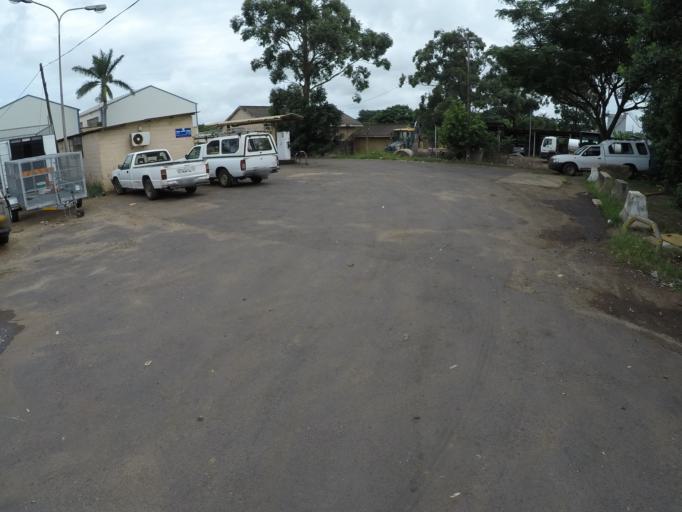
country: ZA
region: KwaZulu-Natal
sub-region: uThungulu District Municipality
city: Empangeni
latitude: -28.7753
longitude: 31.9034
